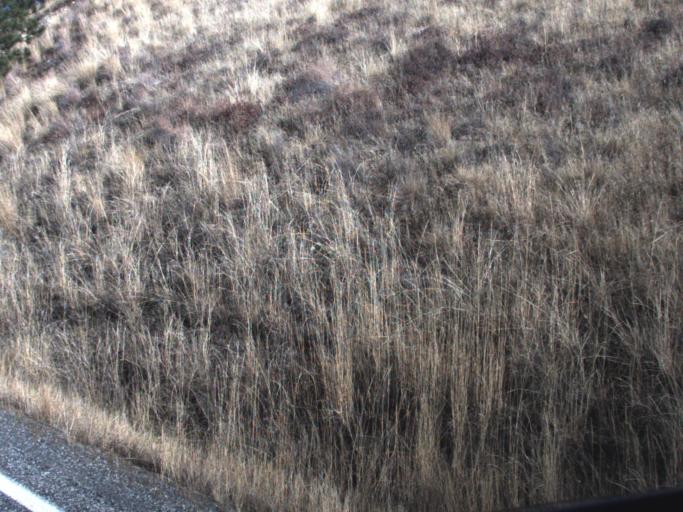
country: CA
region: British Columbia
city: Grand Forks
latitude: 48.8690
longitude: -118.6070
